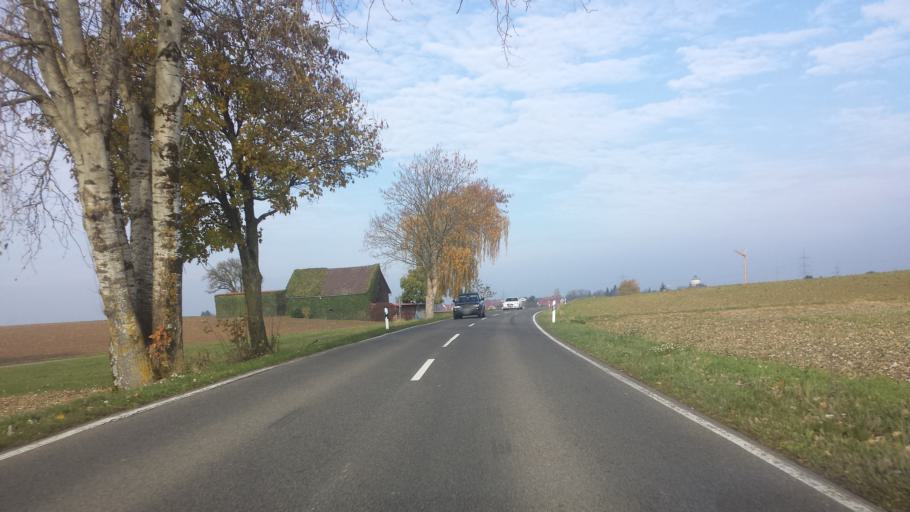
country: DE
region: Baden-Wuerttemberg
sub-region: Karlsruhe Region
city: Huffenhardt
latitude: 49.2848
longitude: 9.0850
